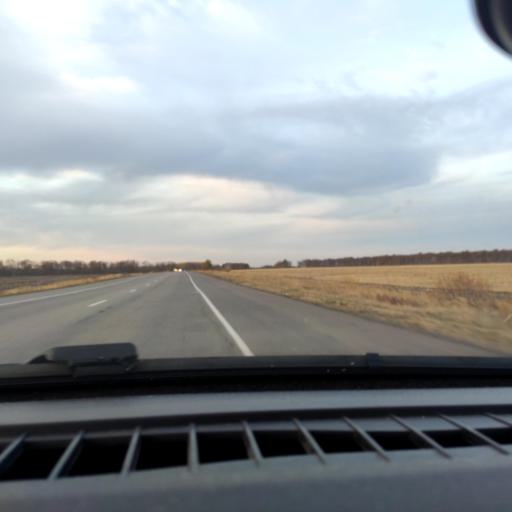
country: RU
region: Voronezj
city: Devitsa
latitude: 51.5834
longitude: 38.9762
